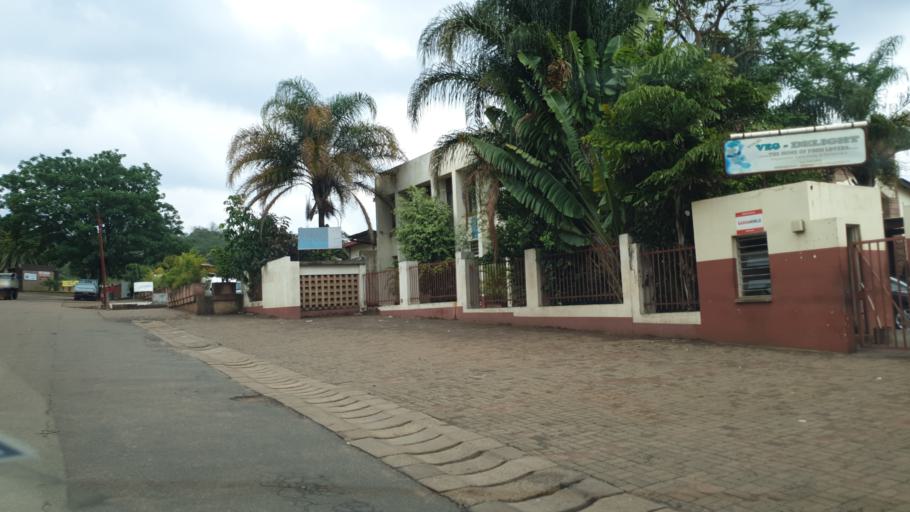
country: MW
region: Central Region
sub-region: Lilongwe District
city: Lilongwe
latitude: -13.9823
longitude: 33.7665
